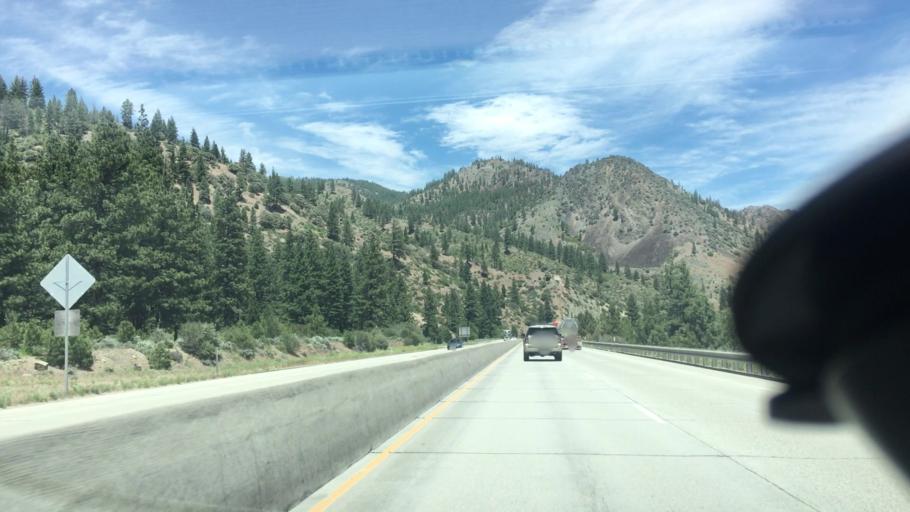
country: US
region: Nevada
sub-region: Washoe County
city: Verdi
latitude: 39.4262
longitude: -120.0352
